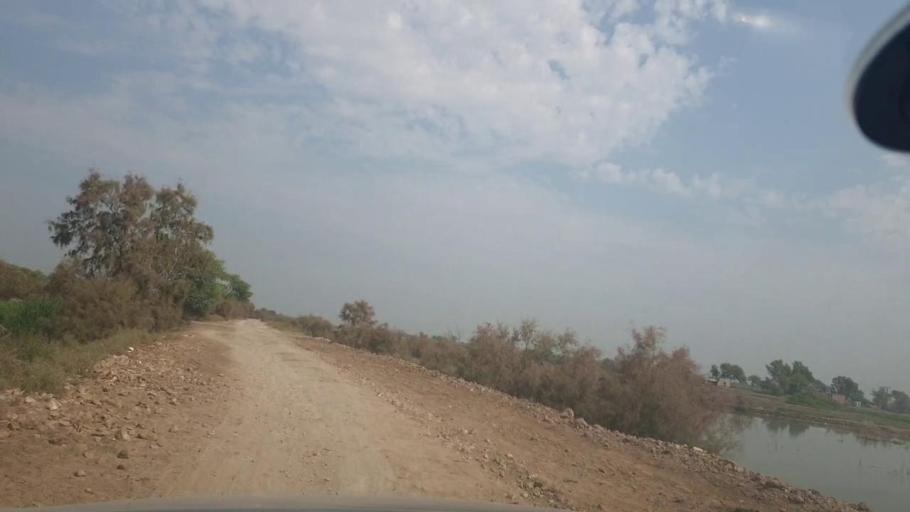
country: PK
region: Balochistan
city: Mehrabpur
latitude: 28.1065
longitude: 68.0913
